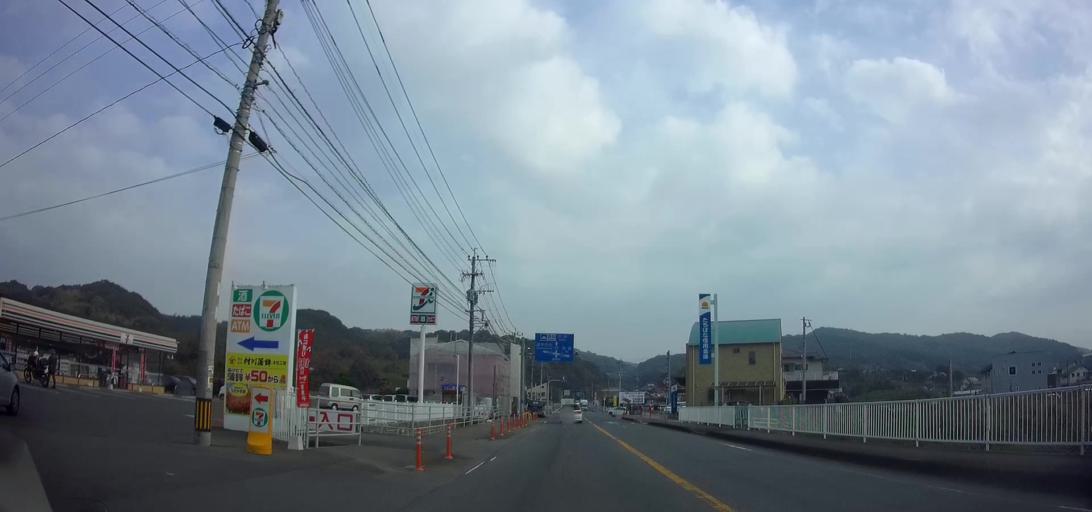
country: JP
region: Nagasaki
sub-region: Isahaya-shi
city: Isahaya
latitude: 32.7972
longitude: 130.0812
